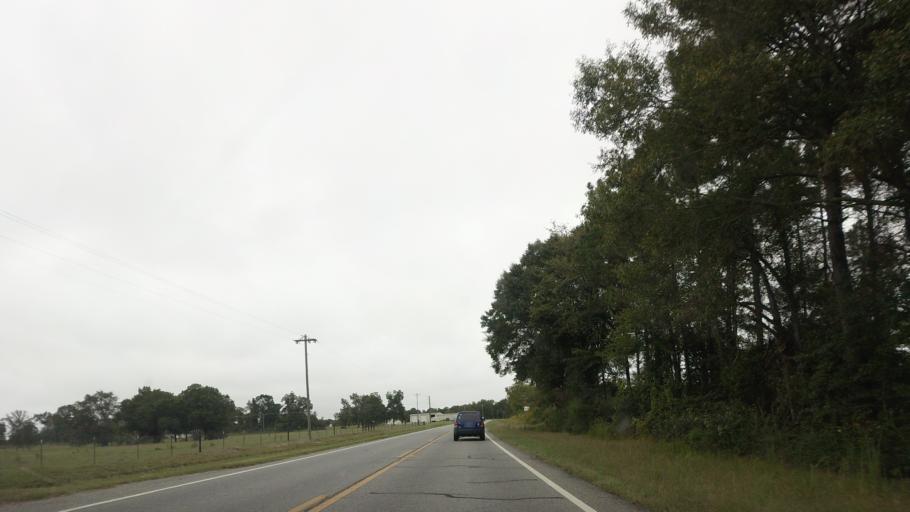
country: US
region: Georgia
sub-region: Irwin County
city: Ocilla
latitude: 31.5753
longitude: -83.2530
